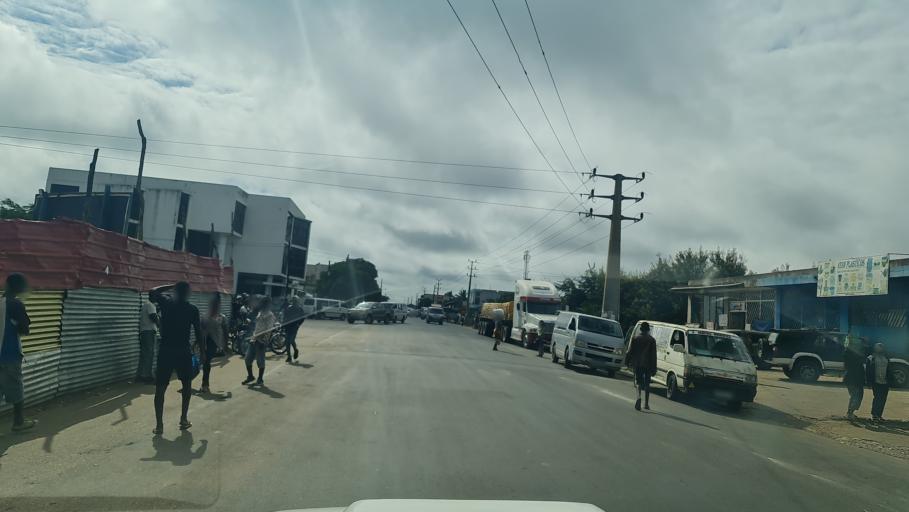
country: MZ
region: Nampula
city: Nampula
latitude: -15.1117
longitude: 39.2273
